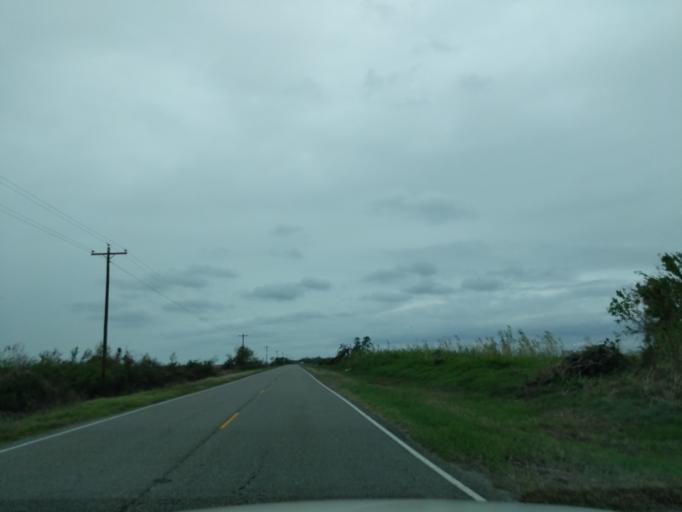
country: US
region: Louisiana
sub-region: Cameron Parish
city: Cameron
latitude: 29.7866
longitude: -93.1614
